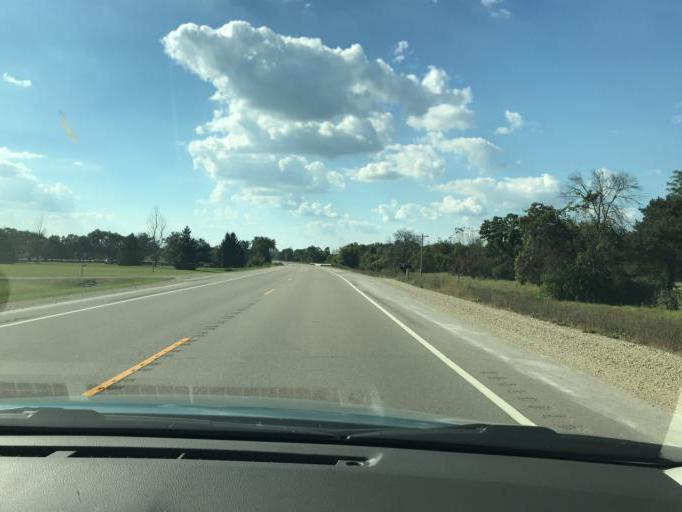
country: US
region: Wisconsin
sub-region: Green County
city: Brodhead
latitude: 42.5704
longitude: -89.3467
